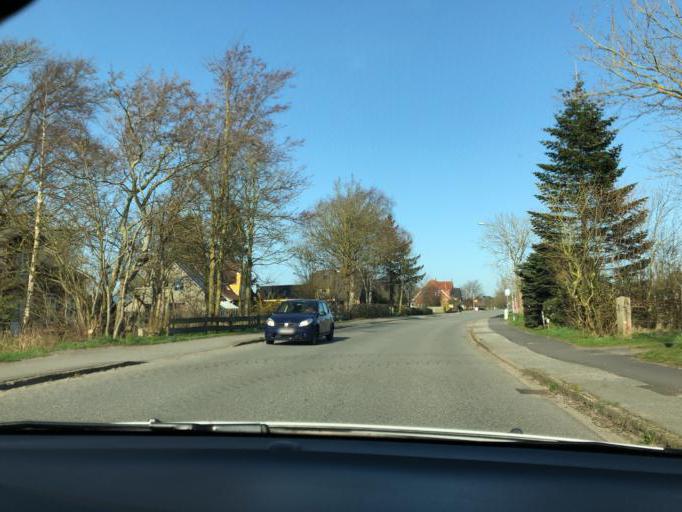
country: DE
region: Schleswig-Holstein
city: Bargum
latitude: 54.6861
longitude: 8.9497
